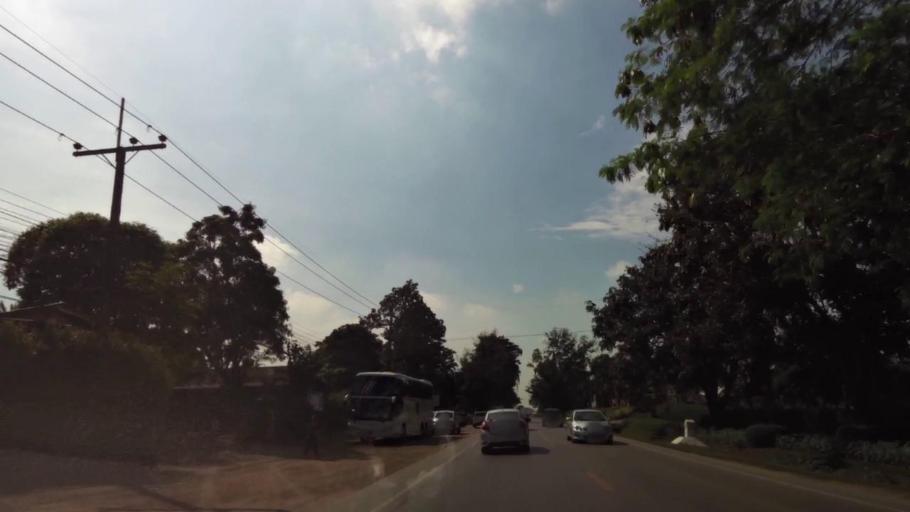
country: TH
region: Chiang Rai
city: Chiang Rai
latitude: 19.8667
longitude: 99.7757
